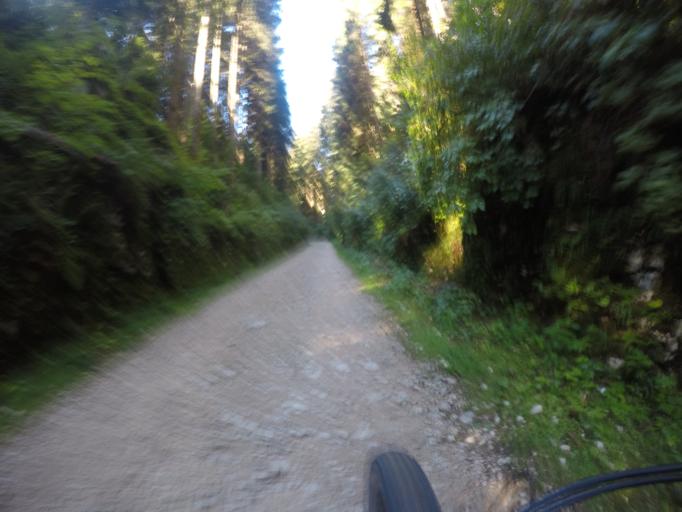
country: IT
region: Veneto
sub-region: Provincia di Vicenza
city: Canove di Roana
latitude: 45.8461
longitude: 11.4689
